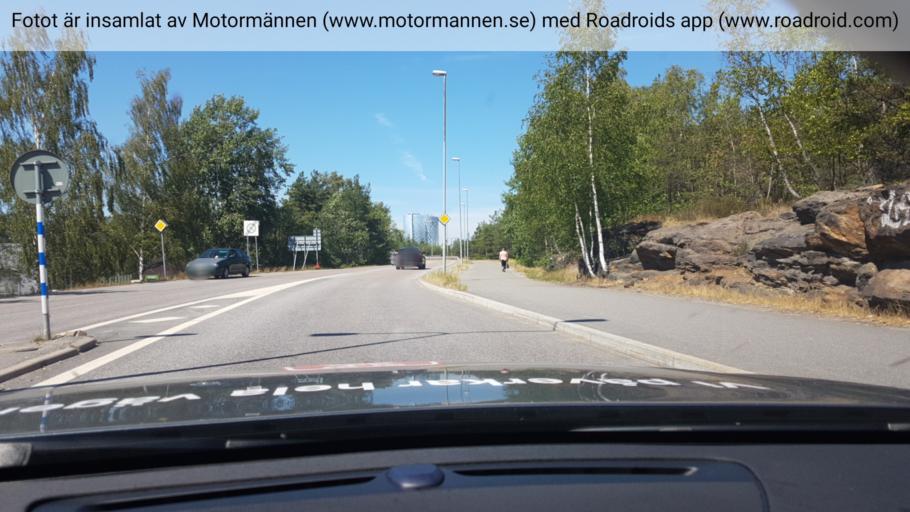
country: SE
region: Stockholm
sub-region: Haninge Kommun
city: Haninge
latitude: 59.1673
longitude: 18.1621
